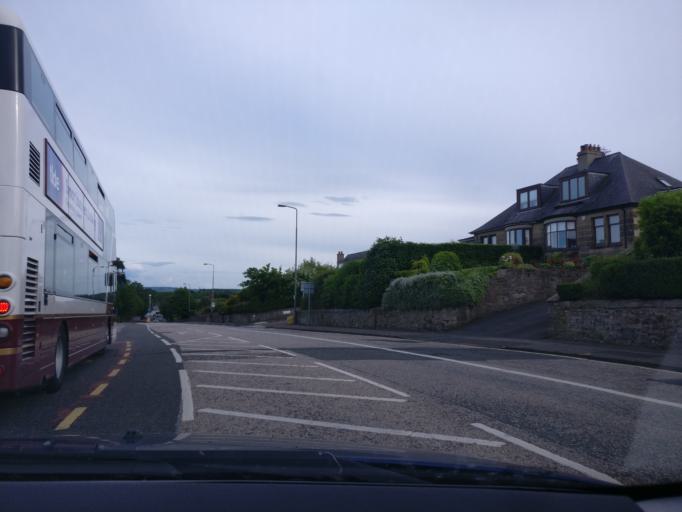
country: GB
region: Scotland
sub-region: West Lothian
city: Seafield
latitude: 55.9503
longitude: -3.1405
